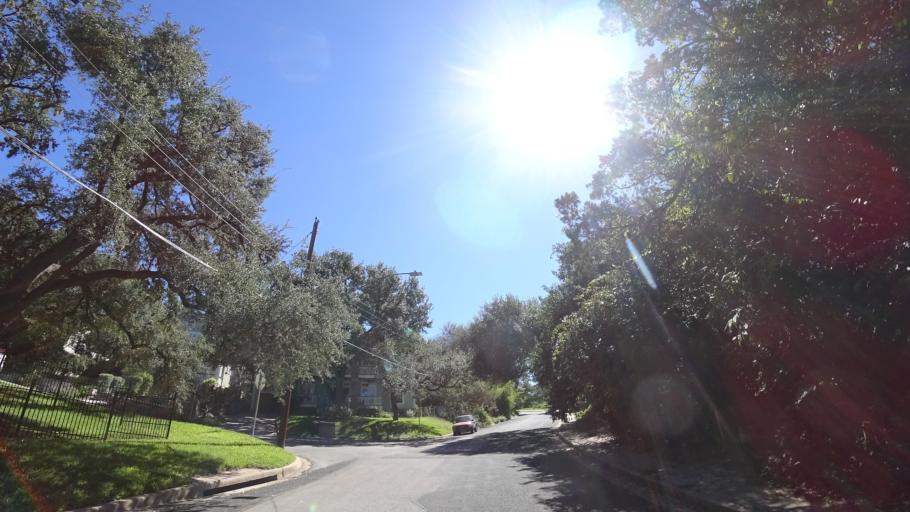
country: US
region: Texas
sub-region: Travis County
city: Austin
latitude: 30.2420
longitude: -97.7444
